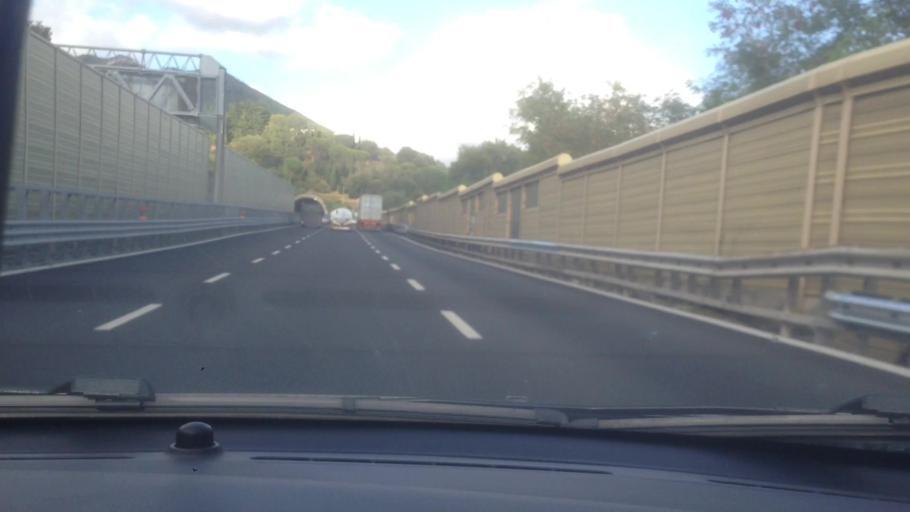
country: IT
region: Liguria
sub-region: Provincia di Genova
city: Arenzano
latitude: 44.4054
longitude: 8.6748
